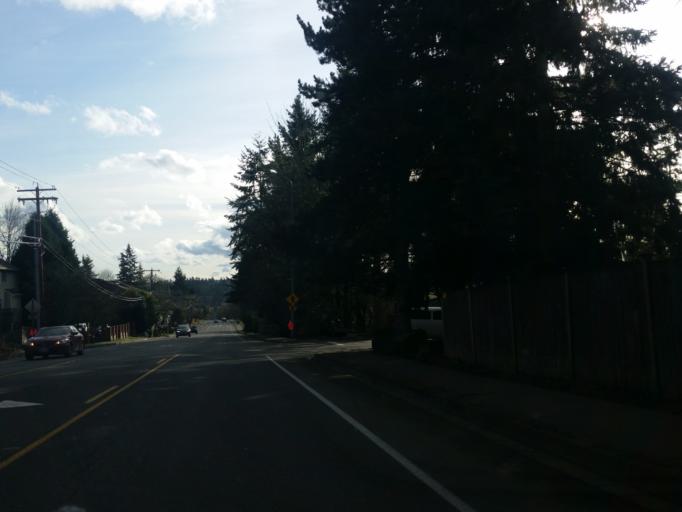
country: US
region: Washington
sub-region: King County
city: Kingsgate
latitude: 47.7213
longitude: -122.1642
